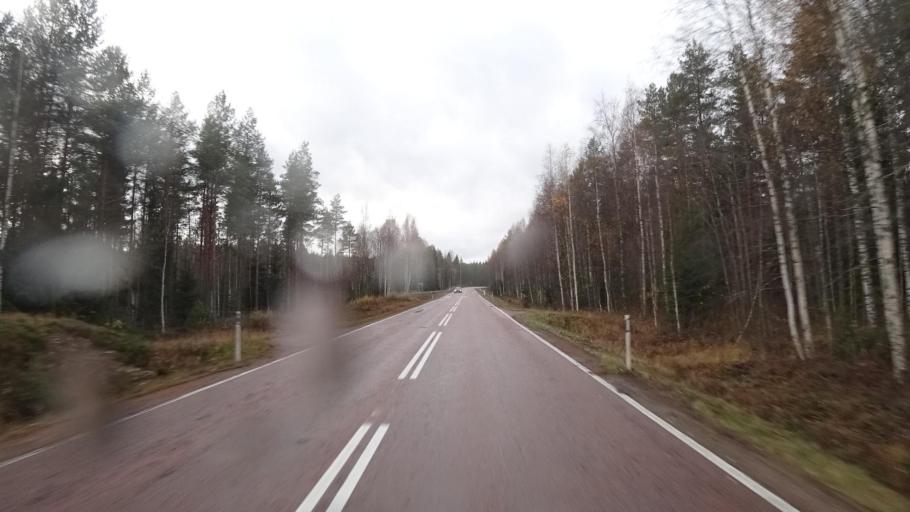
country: FI
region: Southern Savonia
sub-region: Mikkeli
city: Kangasniemi
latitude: 62.0748
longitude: 26.6880
